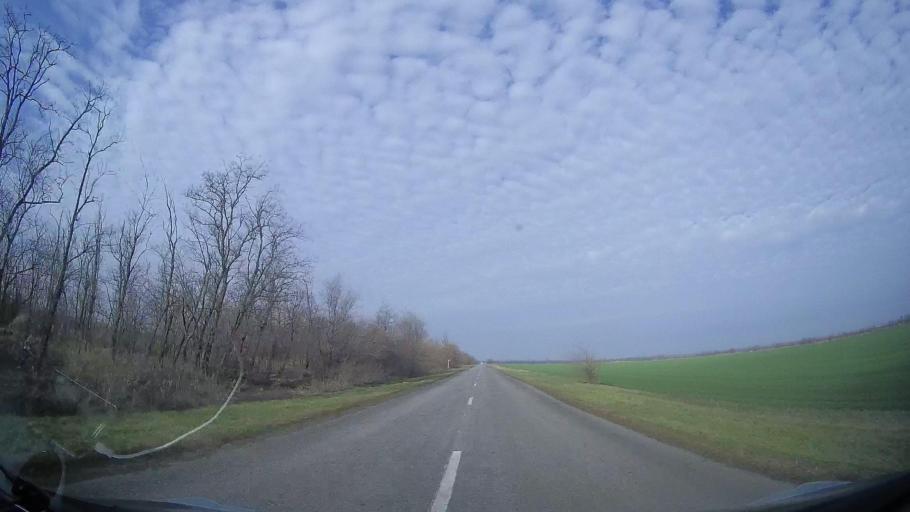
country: RU
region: Rostov
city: Gigant
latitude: 46.8688
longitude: 41.2757
